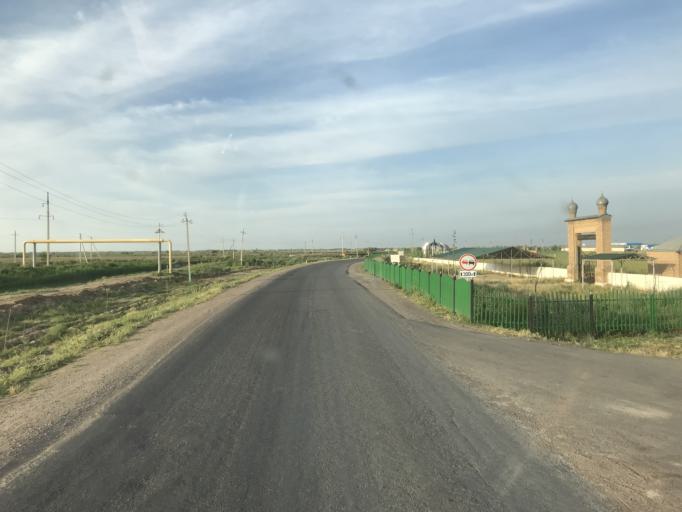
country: KZ
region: Ongtustik Qazaqstan
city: Asykata
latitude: 40.9063
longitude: 68.3666
